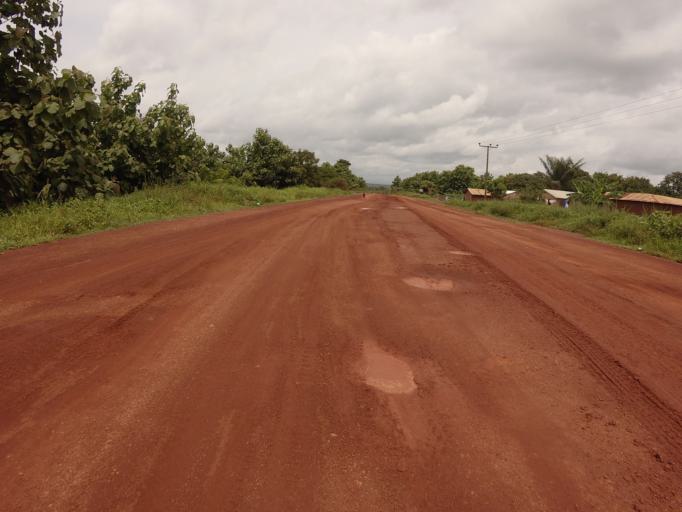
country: GH
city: Kpandae
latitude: 8.4118
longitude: 0.3934
